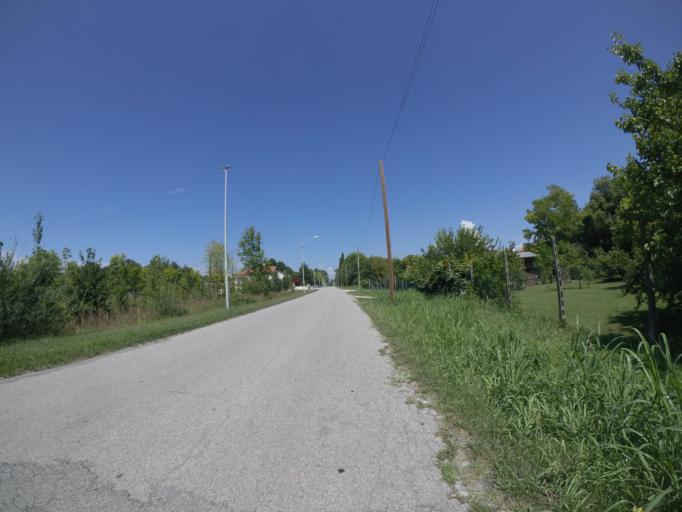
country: IT
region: Friuli Venezia Giulia
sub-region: Provincia di Udine
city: Talmassons
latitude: 45.8816
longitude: 13.1167
